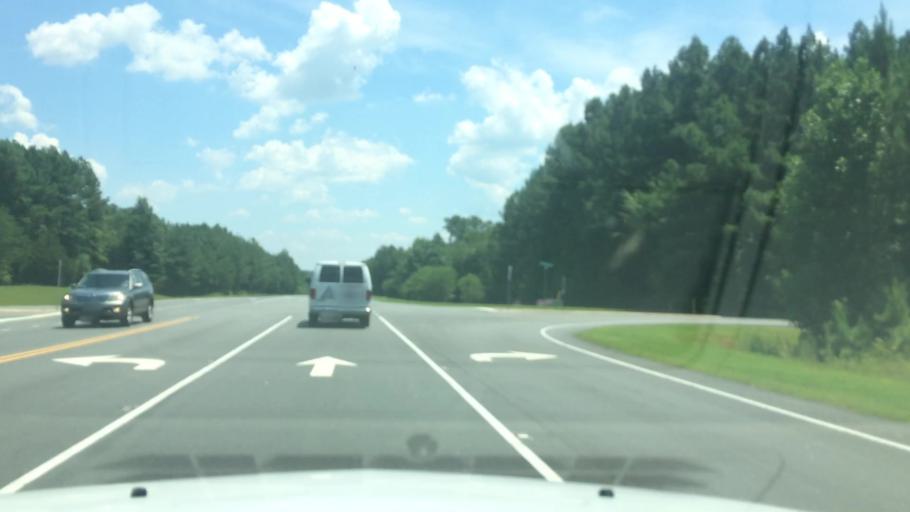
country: US
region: North Carolina
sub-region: Iredell County
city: Statesville
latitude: 35.8093
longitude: -80.9718
